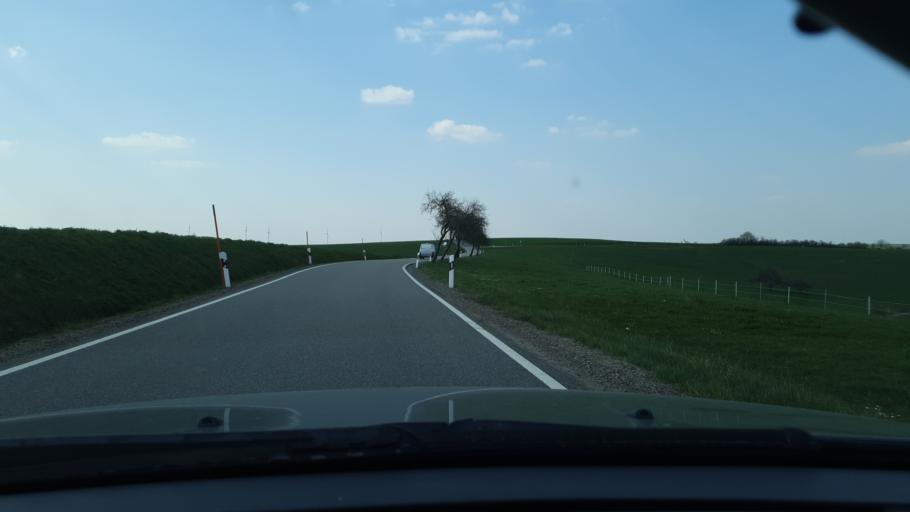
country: DE
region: Rheinland-Pfalz
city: Knopp-Labach
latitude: 49.3358
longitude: 7.4958
